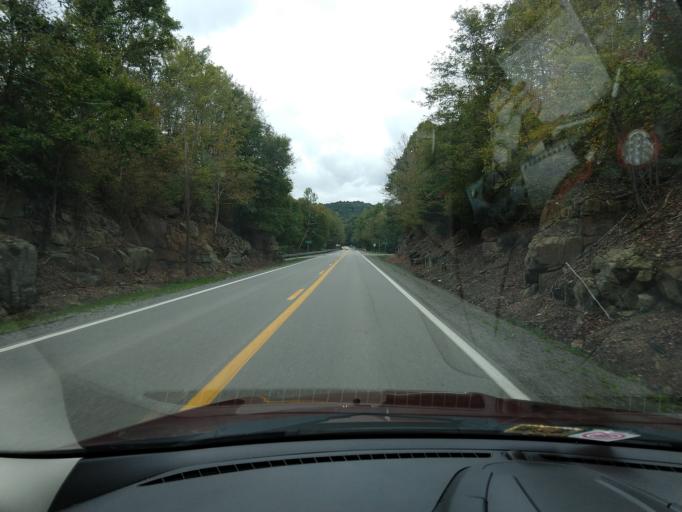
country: US
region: West Virginia
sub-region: Barbour County
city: Philippi
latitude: 39.1229
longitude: -79.9967
